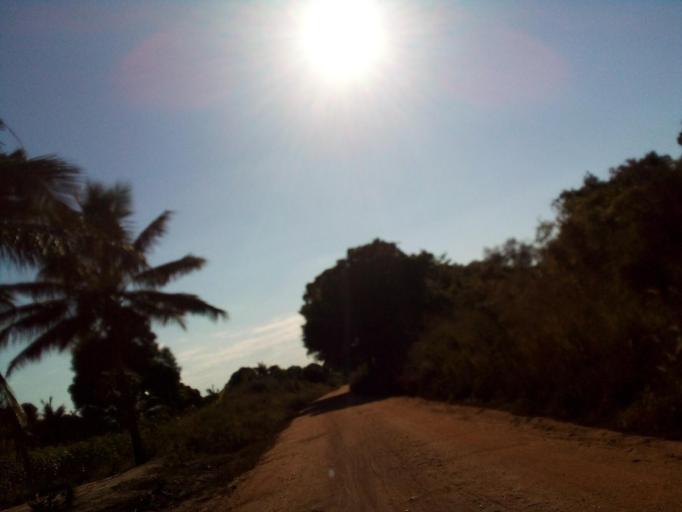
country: MZ
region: Zambezia
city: Quelimane
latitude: -17.5101
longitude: 36.5954
